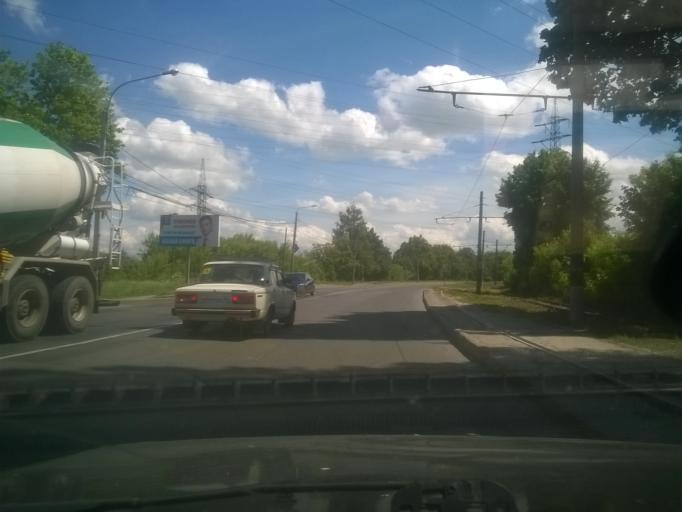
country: RU
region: Kursk
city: Voroshnevo
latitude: 51.6664
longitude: 36.1162
